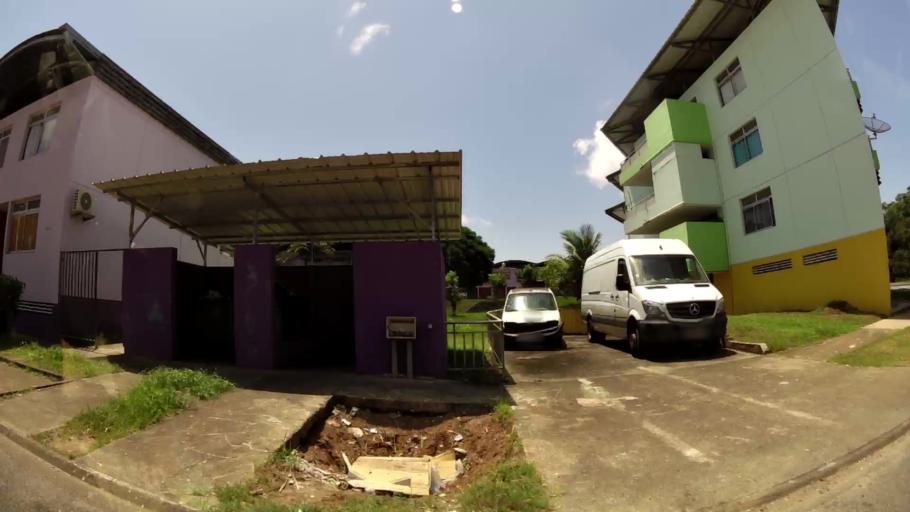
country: GF
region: Guyane
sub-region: Guyane
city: Cayenne
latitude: 4.8990
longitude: -52.3373
